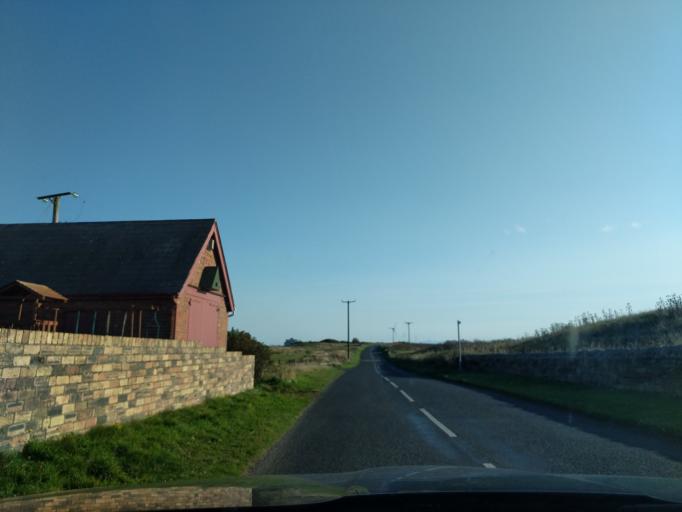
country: GB
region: England
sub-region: Northumberland
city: Lynemouth
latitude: 55.2277
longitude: -1.5291
